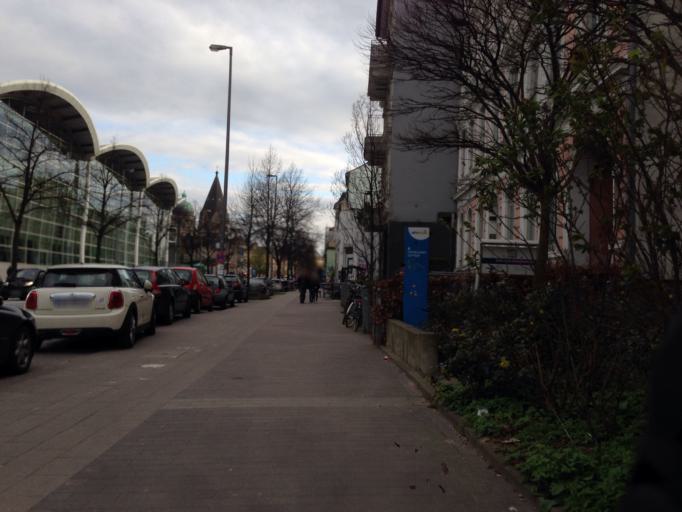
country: DE
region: Hamburg
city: Eimsbuettel
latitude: 53.5602
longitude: 9.9754
